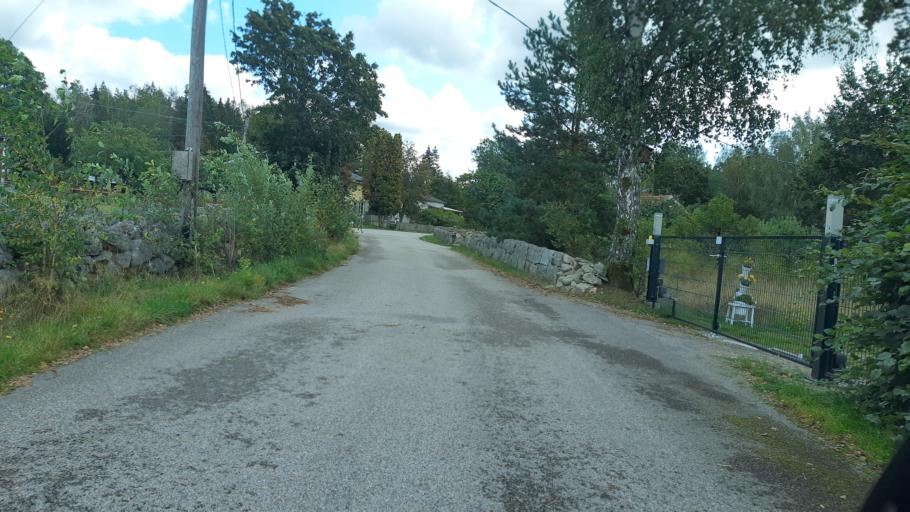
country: SE
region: Kronoberg
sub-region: Tingsryds Kommun
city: Tingsryd
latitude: 56.5041
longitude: 15.1537
